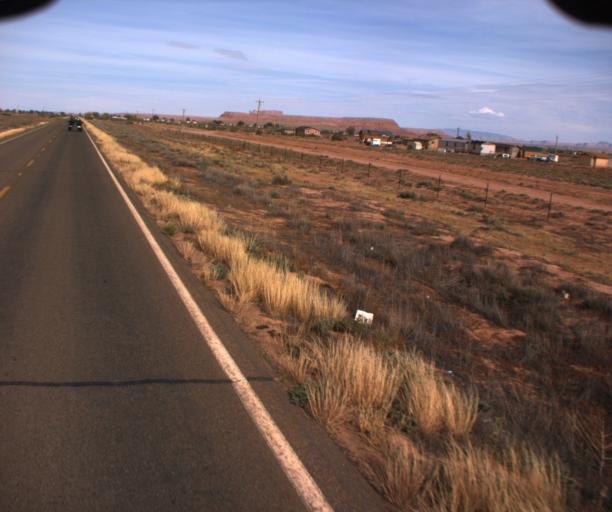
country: US
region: Arizona
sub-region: Apache County
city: Many Farms
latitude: 36.3967
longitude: -109.6095
